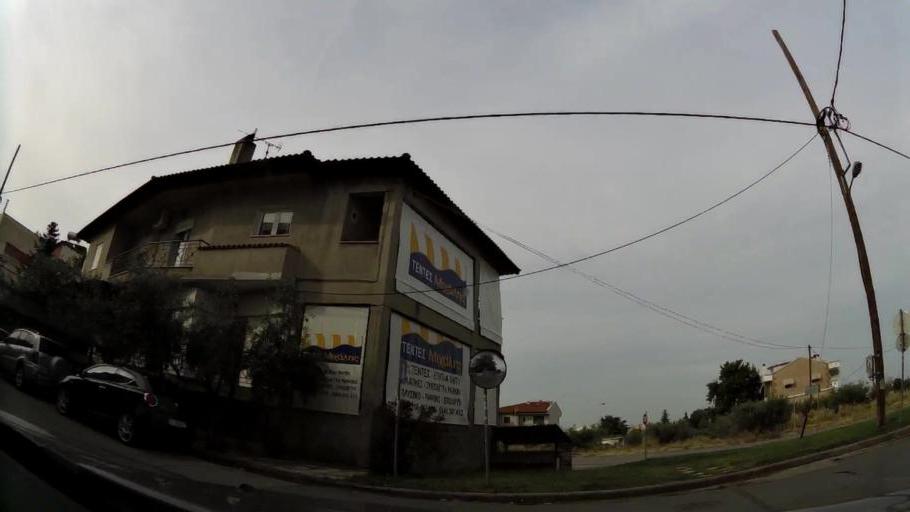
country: GR
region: Central Macedonia
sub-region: Nomos Thessalonikis
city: Thermi
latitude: 40.5466
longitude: 23.0151
